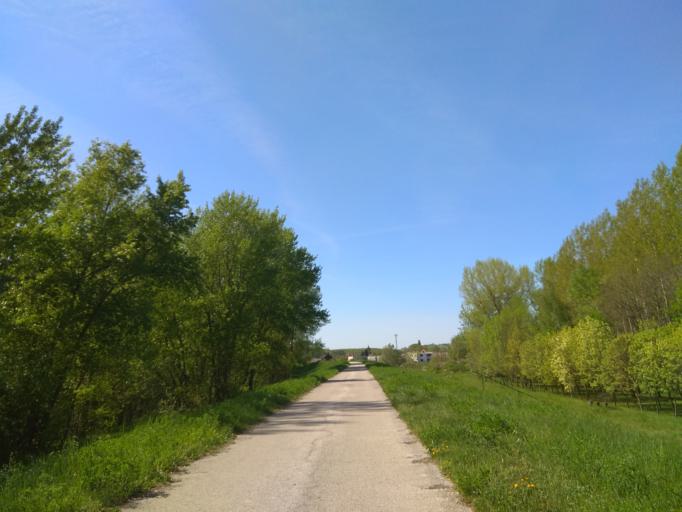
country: HU
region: Gyor-Moson-Sopron
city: Gyor
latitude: 47.7954
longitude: 17.6671
